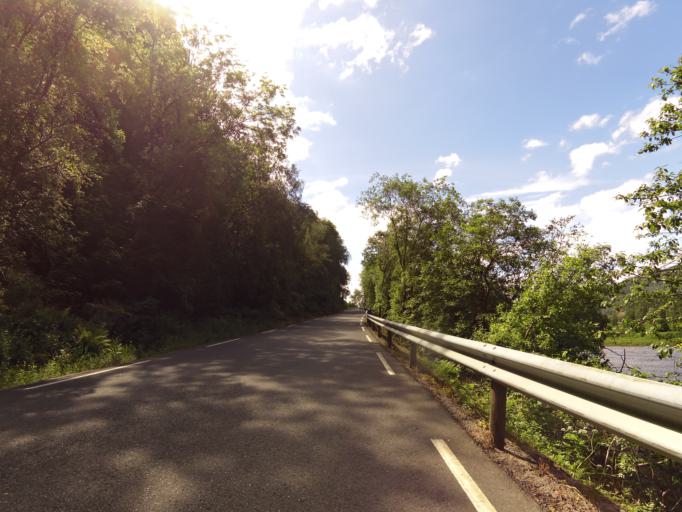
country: NO
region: Vest-Agder
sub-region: Kvinesdal
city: Liknes
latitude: 58.3002
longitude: 6.9533
